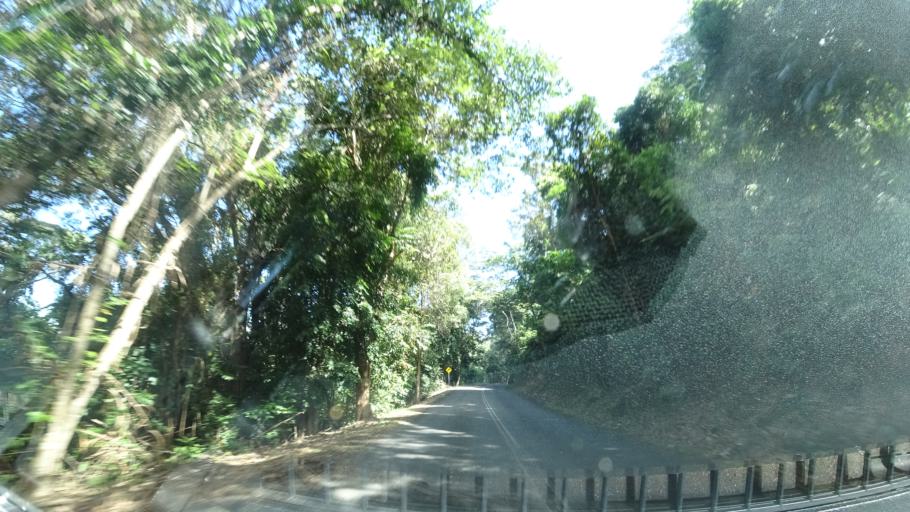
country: AU
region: Queensland
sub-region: Cairns
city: Port Douglas
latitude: -16.2624
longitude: 145.4305
